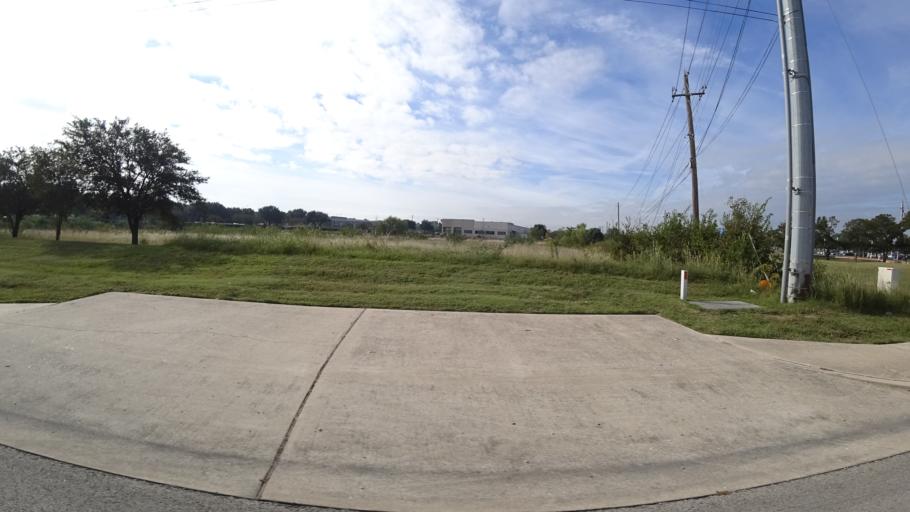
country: US
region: Texas
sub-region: Travis County
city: Austin
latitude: 30.2130
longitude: -97.7207
